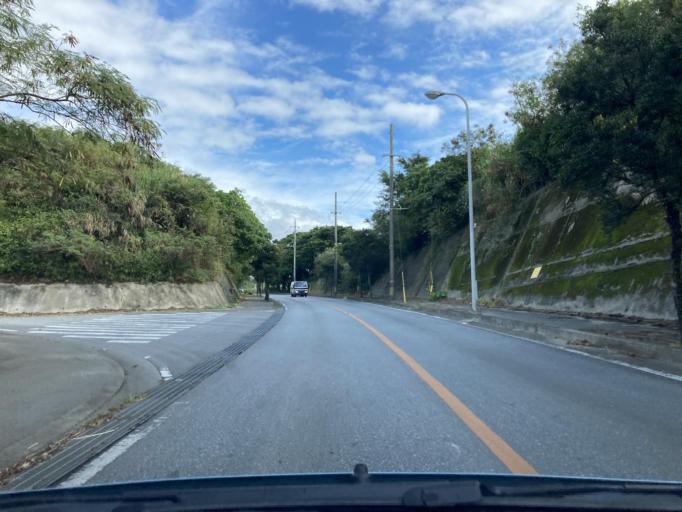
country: JP
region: Okinawa
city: Itoman
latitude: 26.1276
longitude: 127.7113
